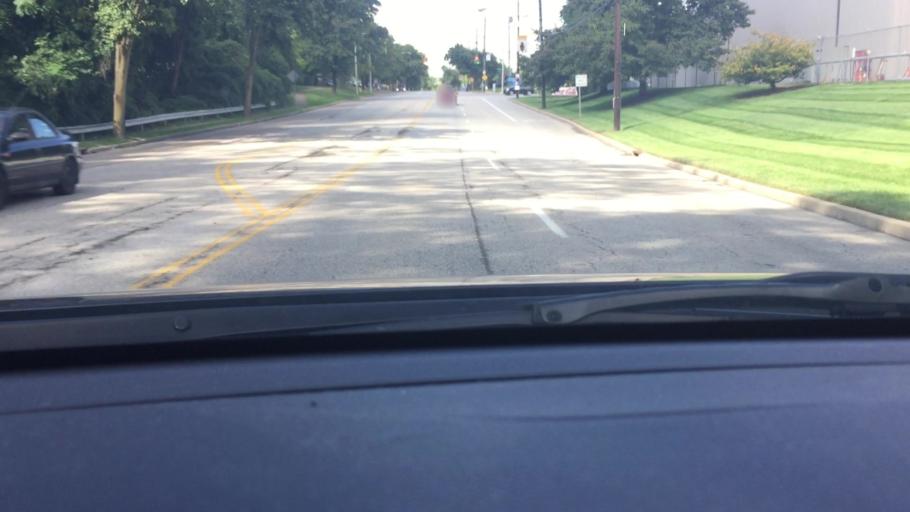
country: US
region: Ohio
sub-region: Hamilton County
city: Fairfax
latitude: 39.1646
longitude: -84.4059
